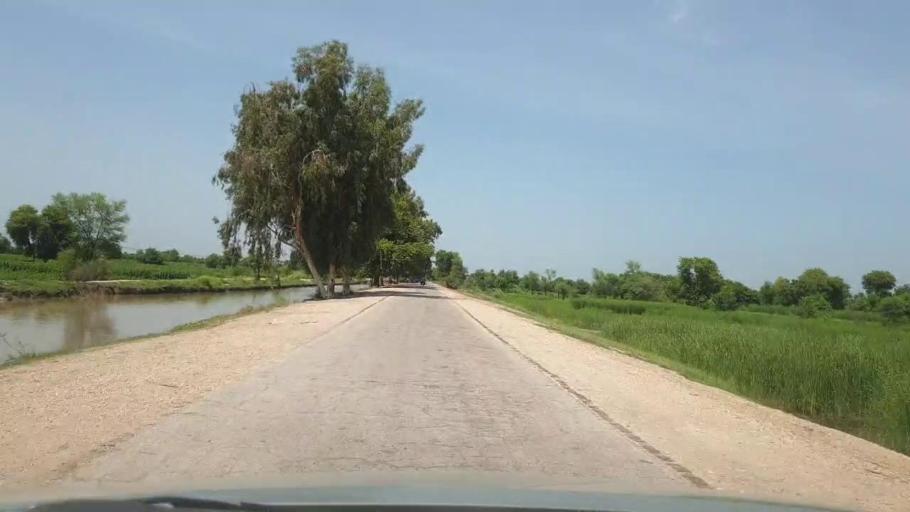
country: PK
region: Sindh
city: Pano Aqil
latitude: 27.6940
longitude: 69.1107
